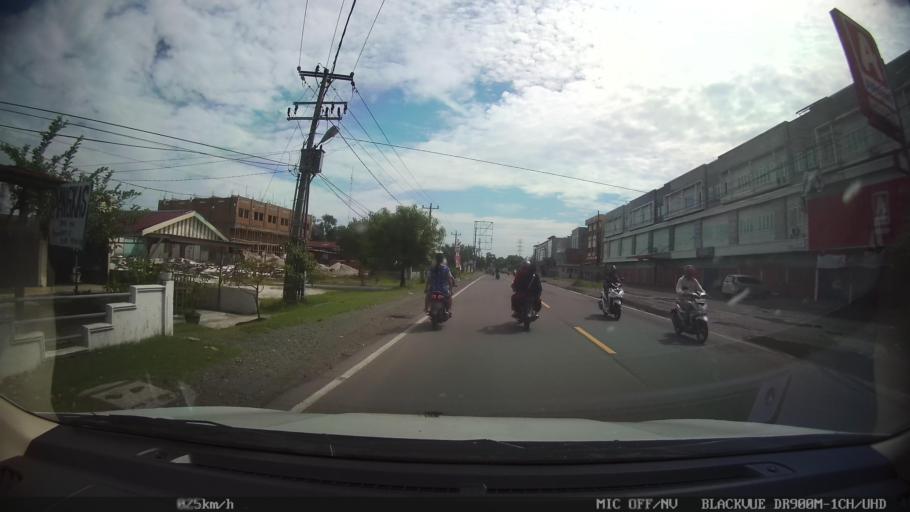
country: ID
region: North Sumatra
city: Medan
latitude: 3.6156
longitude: 98.6519
